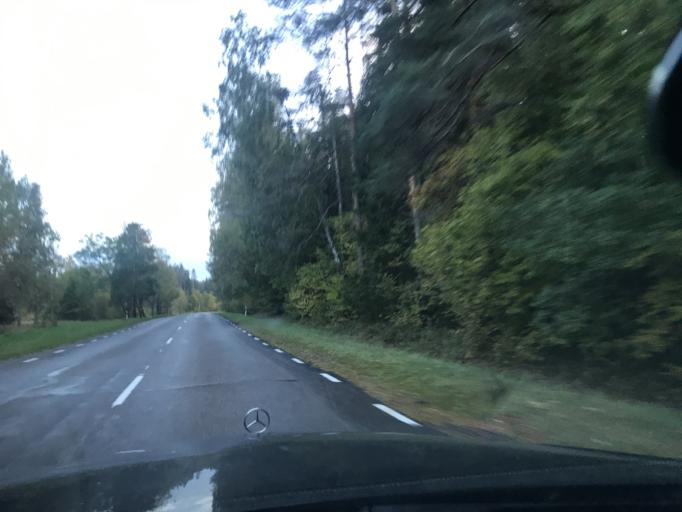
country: EE
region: Valgamaa
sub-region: Torva linn
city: Torva
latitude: 58.0012
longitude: 26.0798
